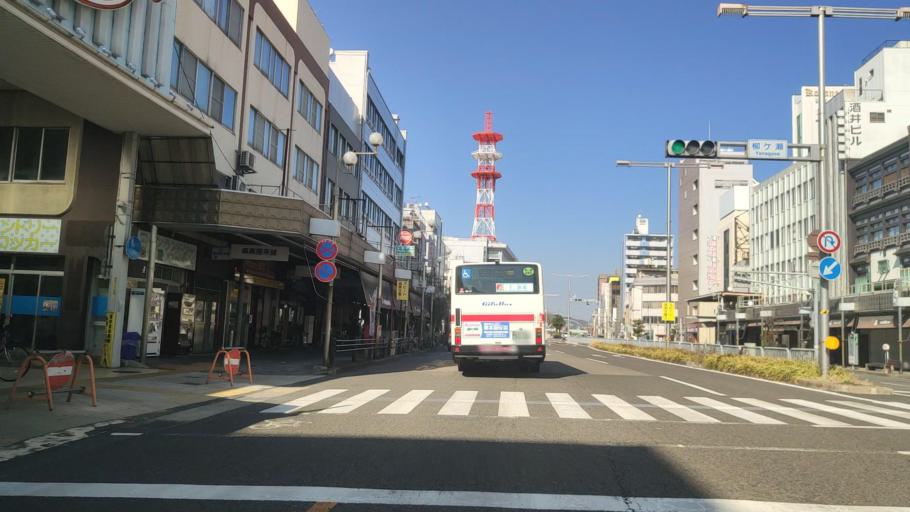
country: JP
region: Gifu
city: Gifu-shi
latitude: 35.4193
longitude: 136.7572
